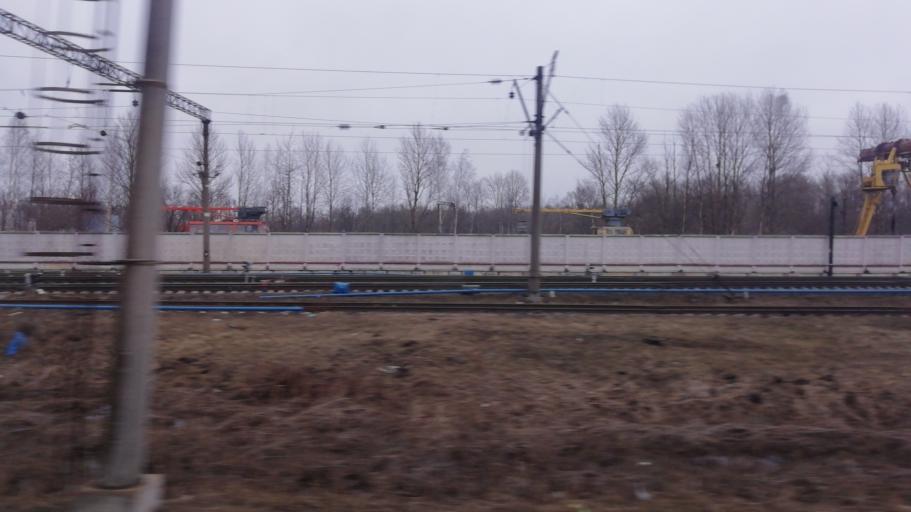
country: RU
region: St.-Petersburg
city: Kupchino
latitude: 59.8810
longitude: 30.3484
